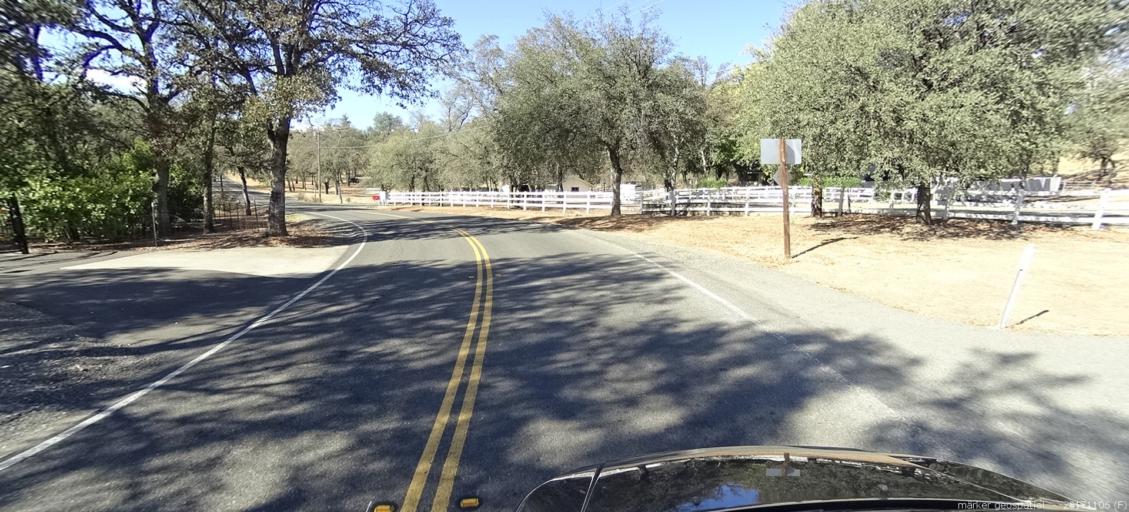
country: US
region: California
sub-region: Shasta County
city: Palo Cedro
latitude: 40.5924
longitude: -122.2487
